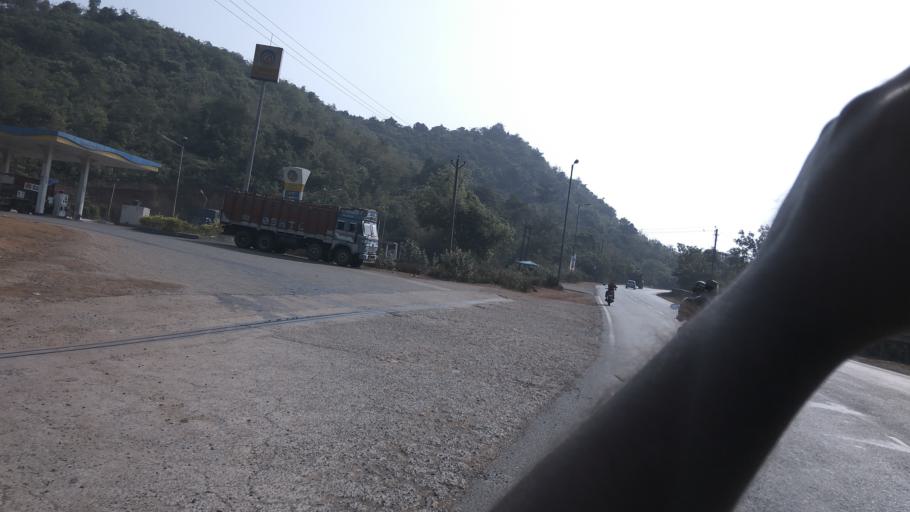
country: IN
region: Goa
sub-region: North Goa
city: Bandora
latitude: 15.4493
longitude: 73.9690
